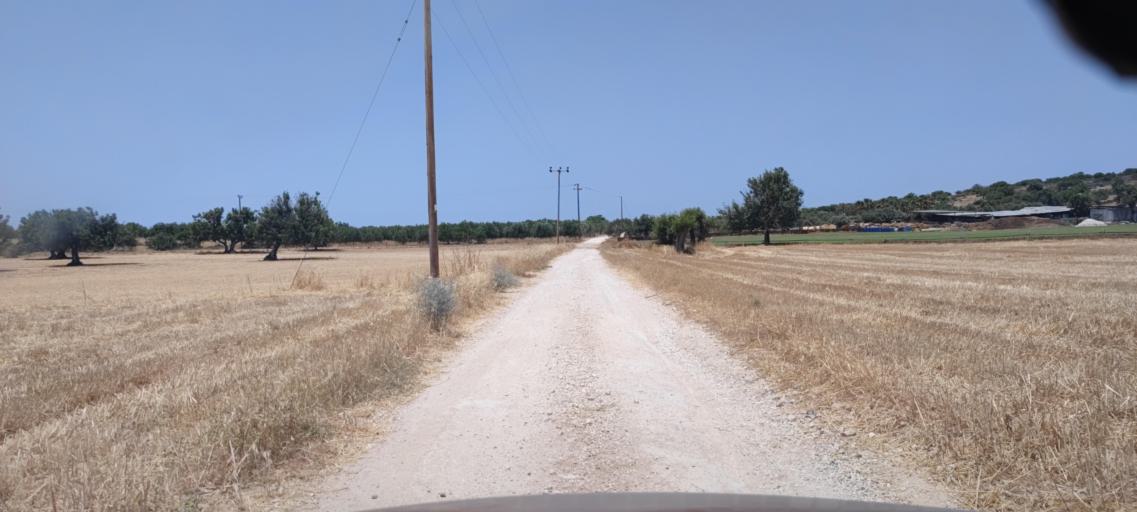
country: CY
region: Limassol
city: Pissouri
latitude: 34.7205
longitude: 32.5939
